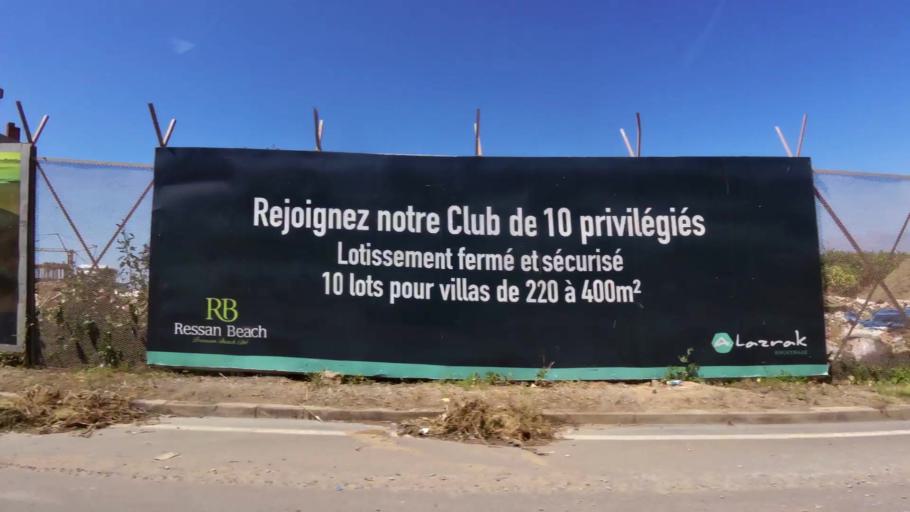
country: MA
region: Grand Casablanca
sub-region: Nouaceur
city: Dar Bouazza
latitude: 33.5322
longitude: -7.8279
